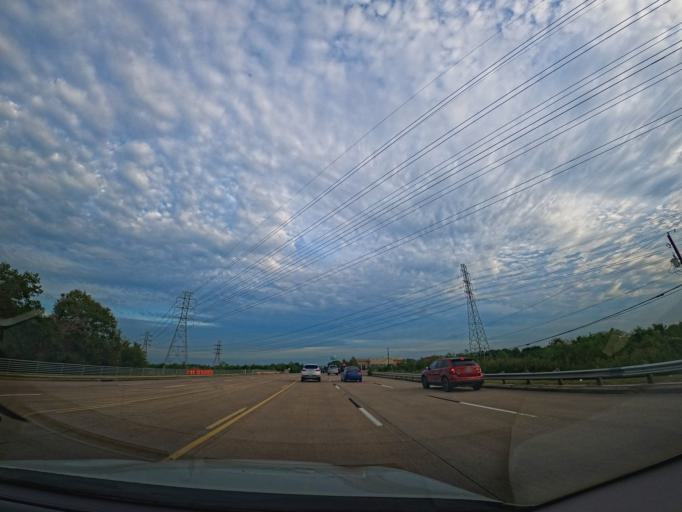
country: US
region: Texas
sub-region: Harris County
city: Nassau Bay
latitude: 29.5288
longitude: -95.0901
